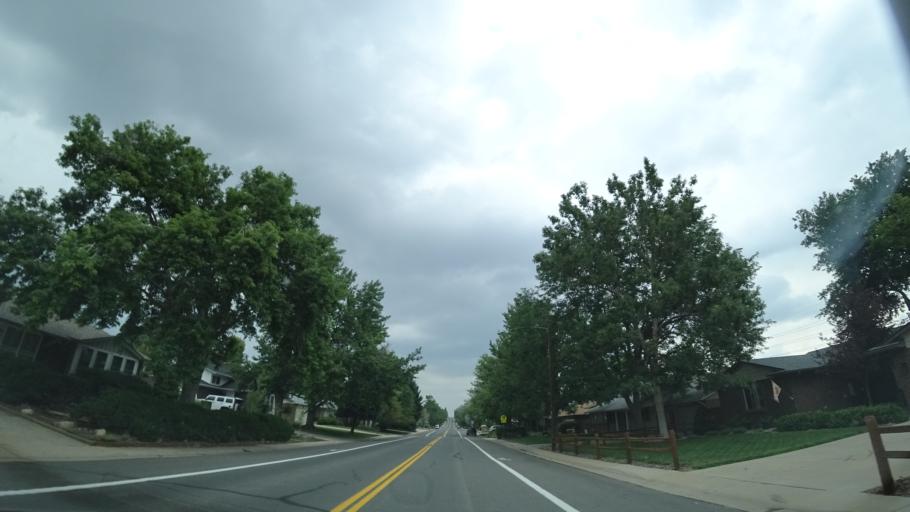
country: US
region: Colorado
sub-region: Jefferson County
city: West Pleasant View
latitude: 39.7010
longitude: -105.1476
